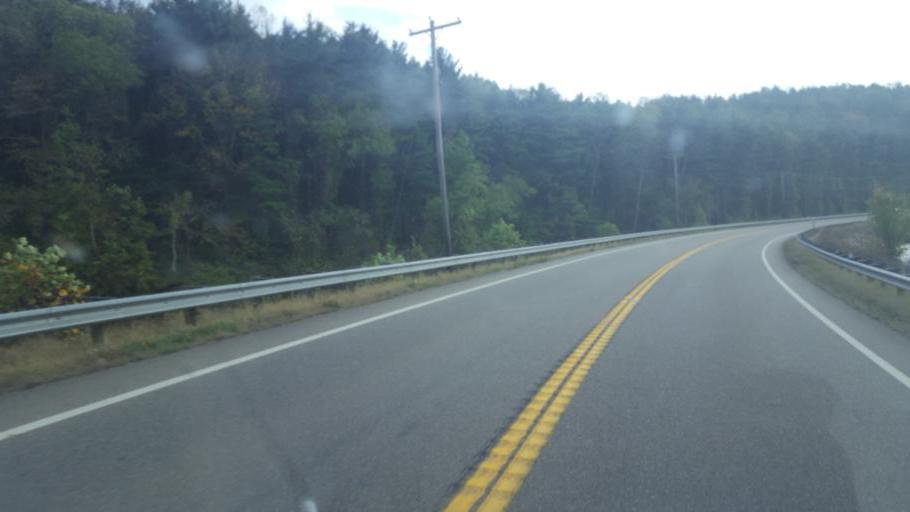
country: US
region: Ohio
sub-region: Tuscarawas County
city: Dennison
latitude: 40.3389
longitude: -81.1869
